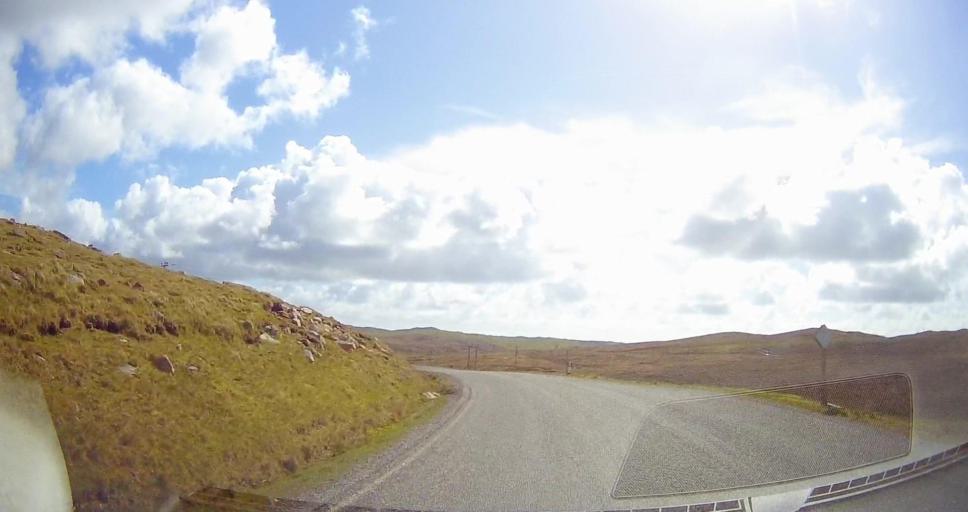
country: GB
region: Scotland
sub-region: Shetland Islands
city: Lerwick
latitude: 60.4829
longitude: -1.4043
